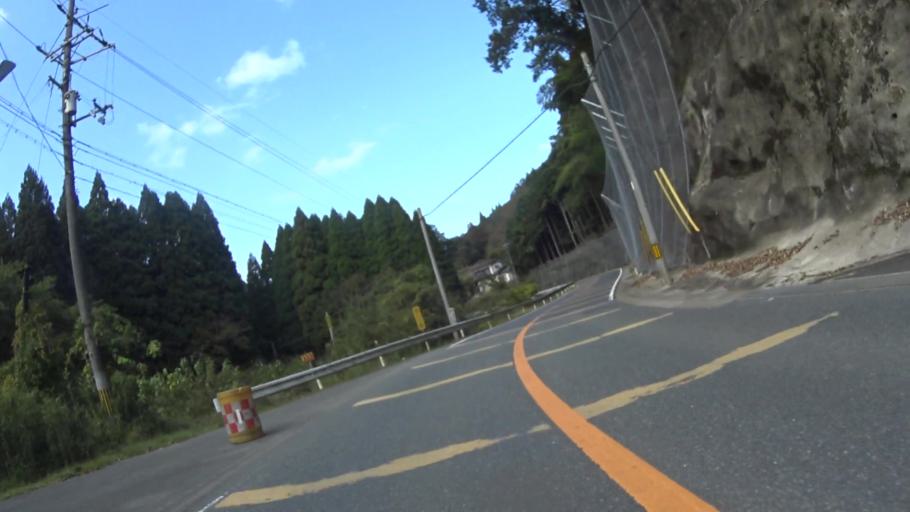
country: JP
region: Kyoto
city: Fukuchiyama
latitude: 35.3448
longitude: 135.0658
